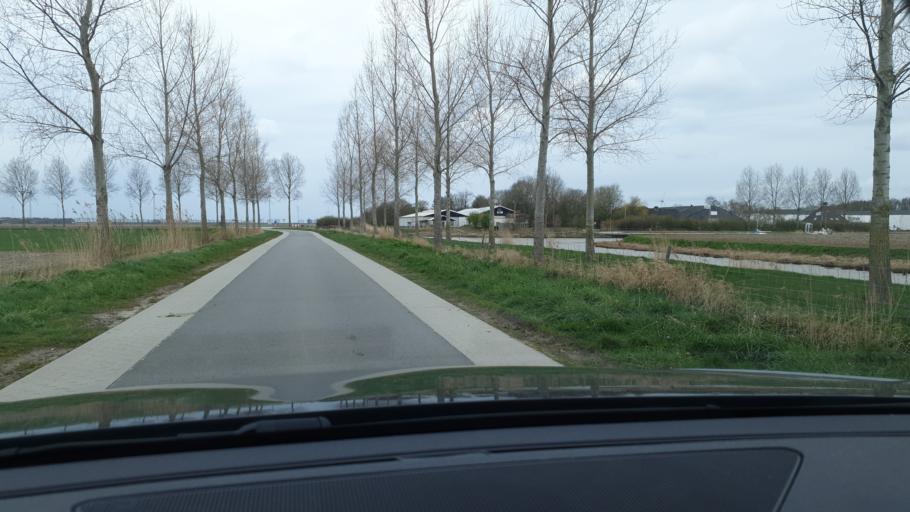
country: NL
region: Flevoland
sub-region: Gemeente Urk
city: Urk
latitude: 52.7168
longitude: 5.6485
